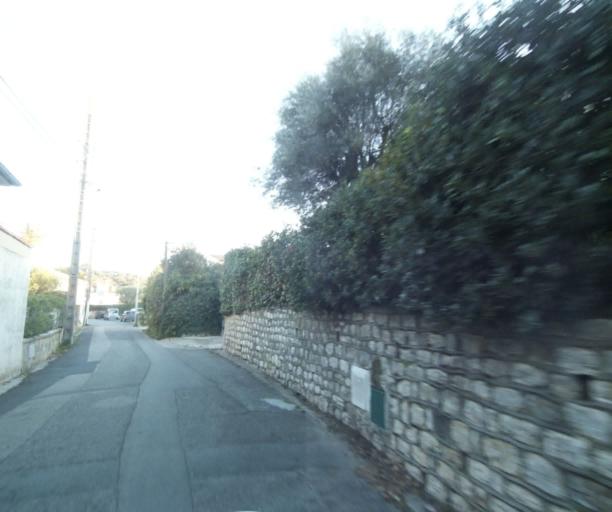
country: FR
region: Provence-Alpes-Cote d'Azur
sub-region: Departement des Alpes-Maritimes
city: Antibes
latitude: 43.5691
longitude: 7.1261
